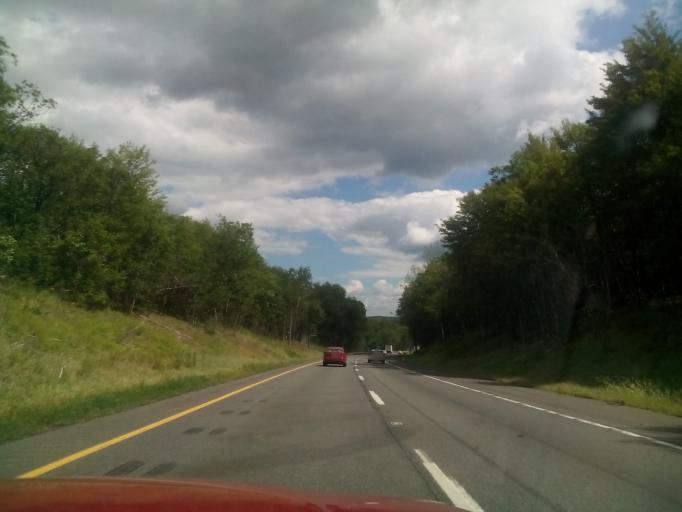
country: US
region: Pennsylvania
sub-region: Monroe County
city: Tannersville
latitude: 41.0611
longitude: -75.3319
